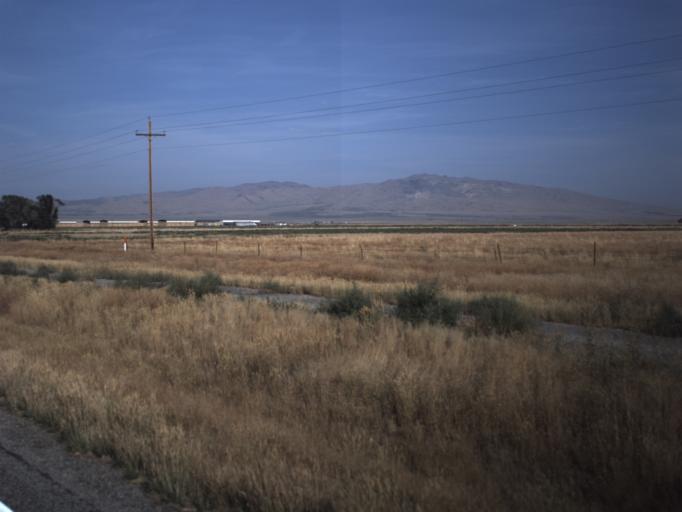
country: US
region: Idaho
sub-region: Oneida County
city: Malad City
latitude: 41.9667
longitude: -112.8906
